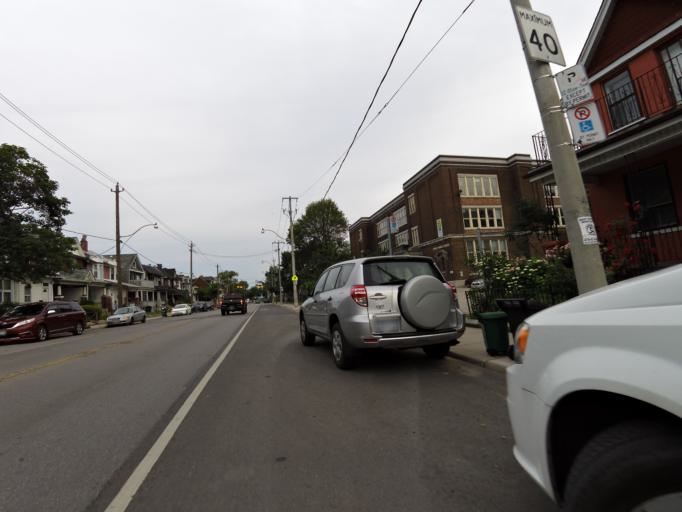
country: CA
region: Ontario
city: Toronto
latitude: 43.6779
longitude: -79.3394
